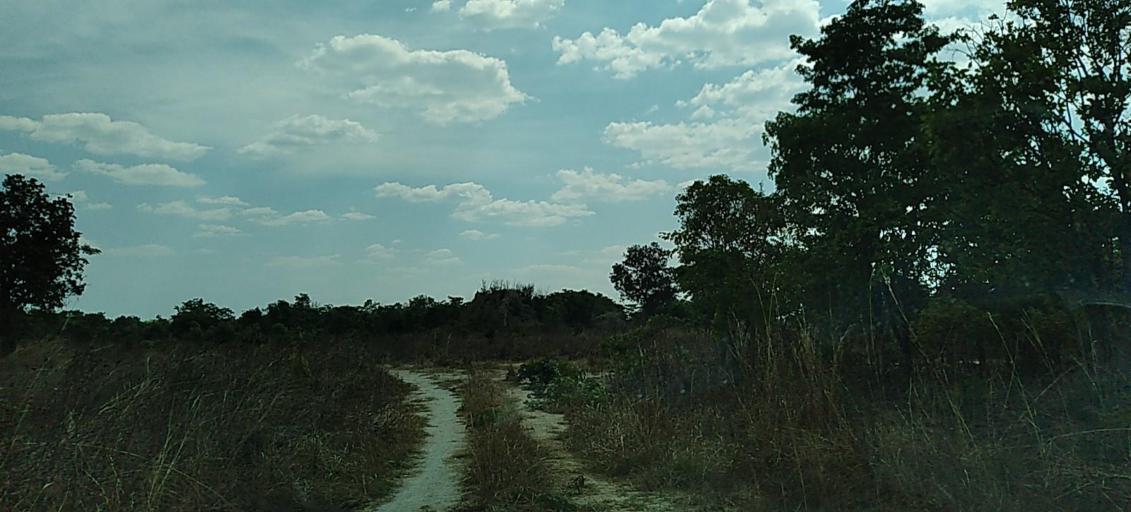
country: ZM
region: Copperbelt
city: Chililabombwe
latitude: -12.3386
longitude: 27.7790
